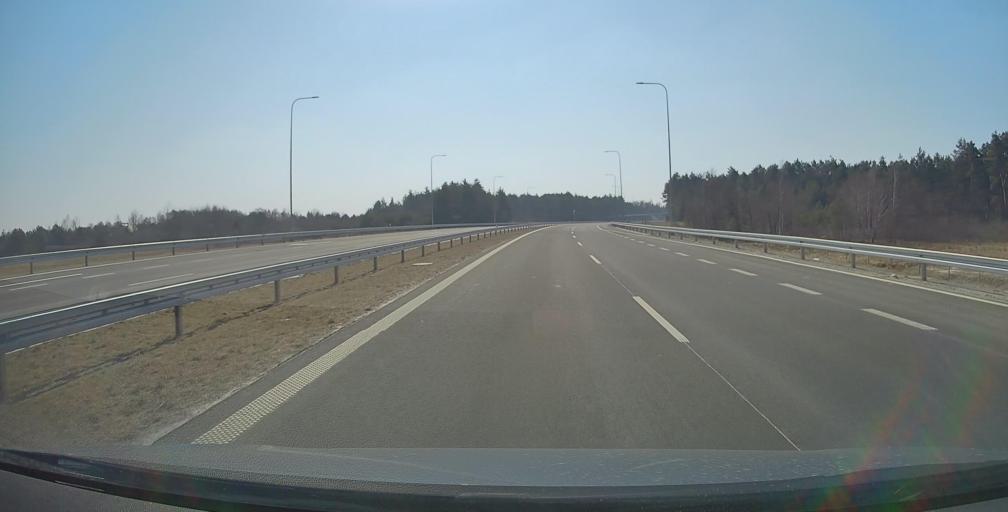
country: PL
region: Lublin Voivodeship
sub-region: Powiat janowski
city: Janow Lubelski
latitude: 50.7125
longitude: 22.3858
